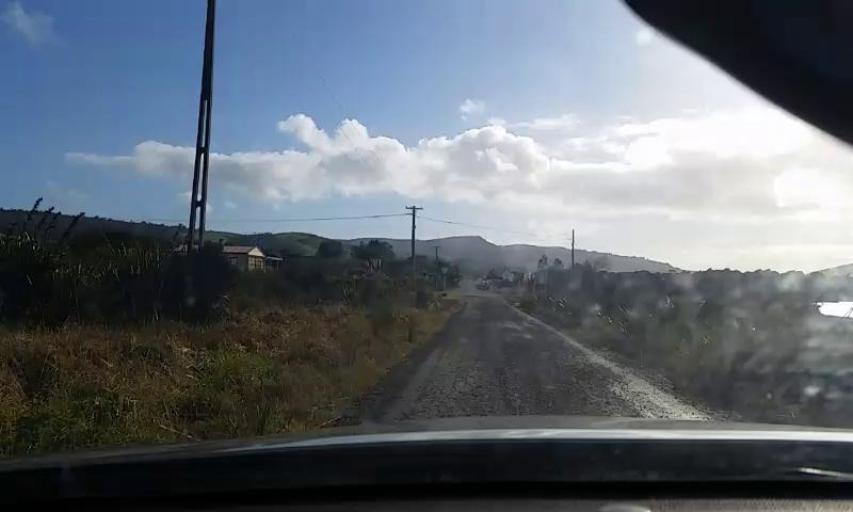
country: NZ
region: Otago
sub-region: Clutha District
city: Papatowai
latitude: -46.6270
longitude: 169.1359
